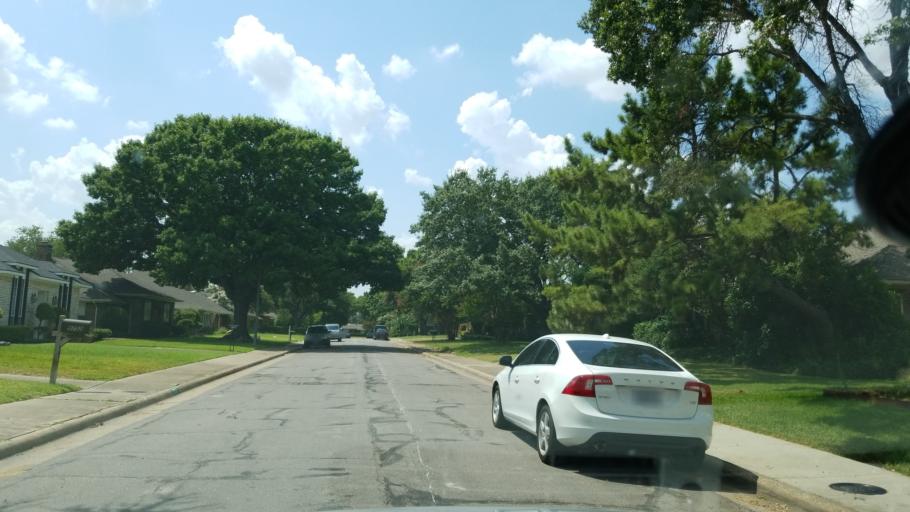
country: US
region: Texas
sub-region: Dallas County
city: Richardson
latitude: 32.9208
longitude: -96.7194
